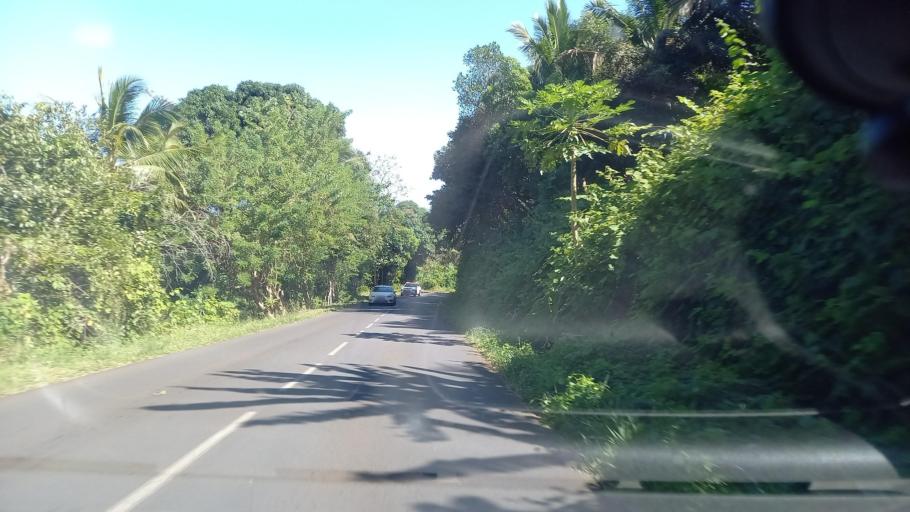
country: YT
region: Tsingoni
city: Tsingoni
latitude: -12.7842
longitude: 45.1467
